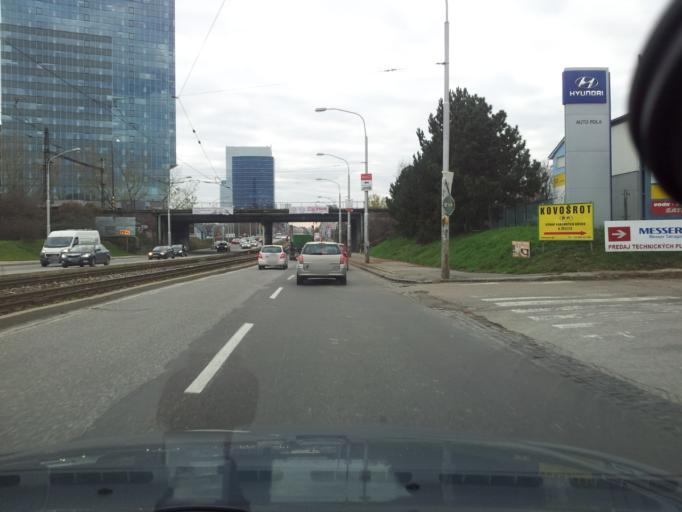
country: SK
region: Bratislavsky
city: Bratislava
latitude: 48.1745
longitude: 17.1437
